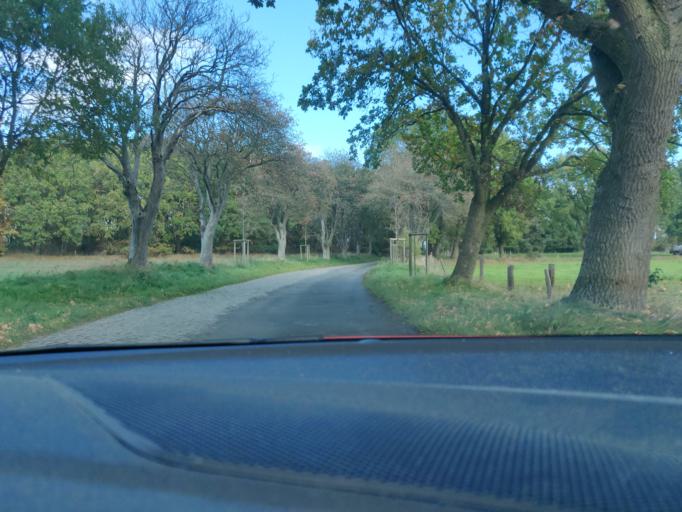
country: DE
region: Lower Saxony
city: Cuxhaven
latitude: 53.8668
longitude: 8.6408
